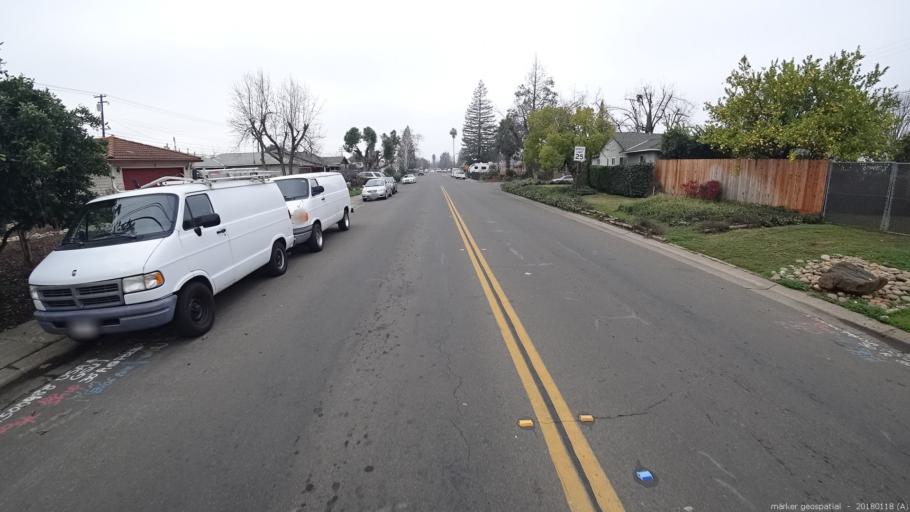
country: US
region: California
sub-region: Sacramento County
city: Rancho Cordova
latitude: 38.5910
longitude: -121.3041
